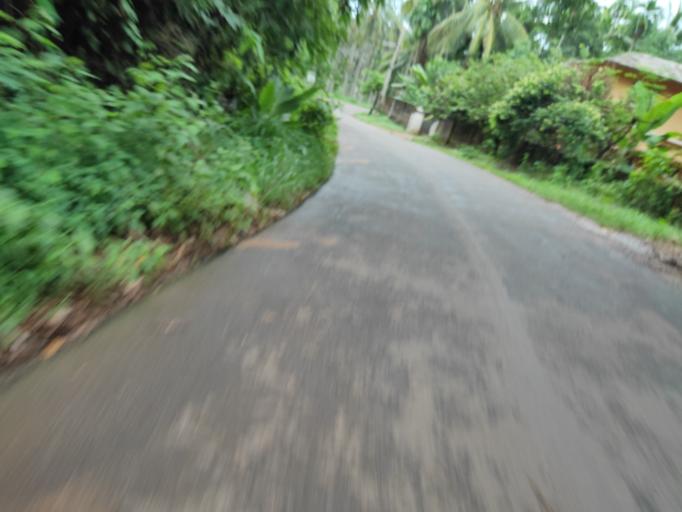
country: IN
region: Kerala
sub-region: Malappuram
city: Manjeri
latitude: 11.1850
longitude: 76.2054
